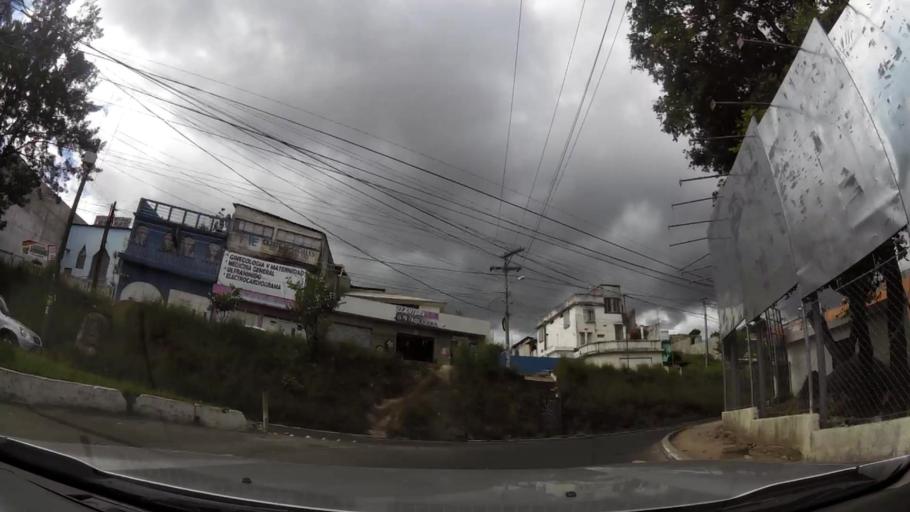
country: GT
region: Guatemala
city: Guatemala City
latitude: 14.6823
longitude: -90.5517
